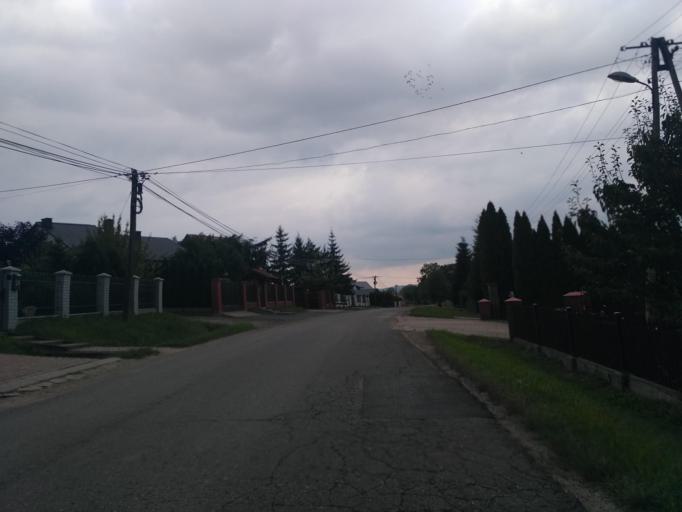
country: PL
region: Subcarpathian Voivodeship
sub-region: Powiat rzeszowski
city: Siedliska
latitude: 49.9641
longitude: 21.9795
